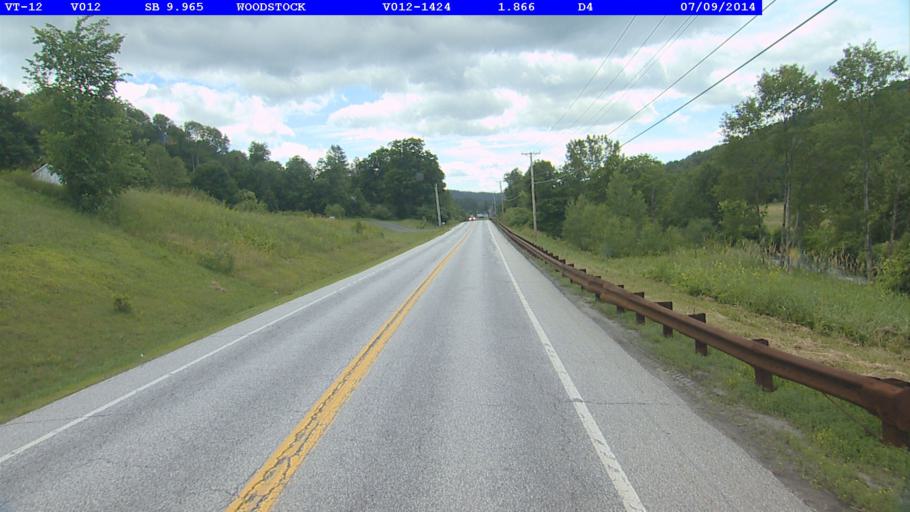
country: US
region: Vermont
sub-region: Windsor County
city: Woodstock
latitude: 43.6459
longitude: -72.5350
